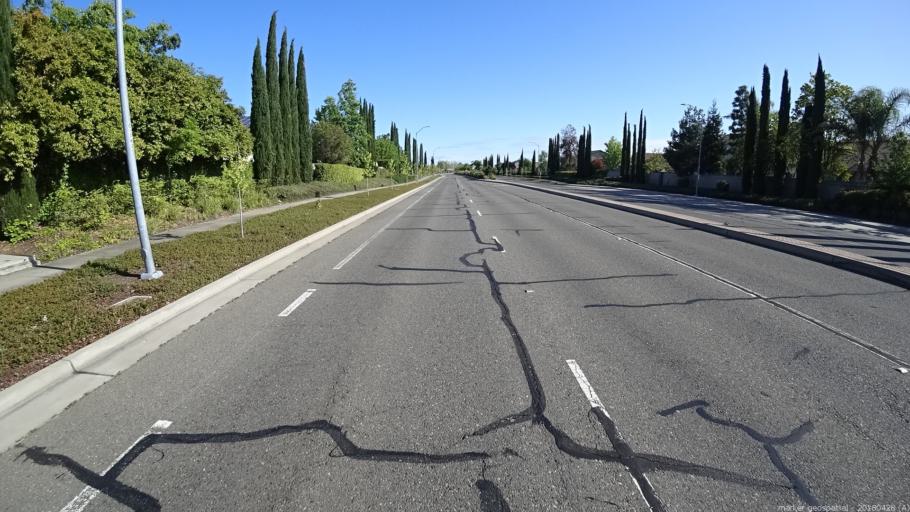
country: US
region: California
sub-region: Yolo County
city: West Sacramento
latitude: 38.5393
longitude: -121.5762
